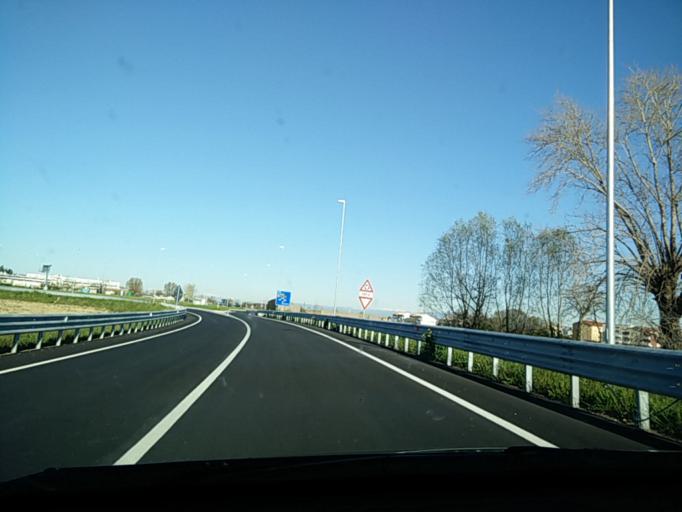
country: IT
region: Veneto
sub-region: Provincia di Venezia
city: Marcon-Gaggio-Colmello
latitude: 45.5487
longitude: 12.2988
